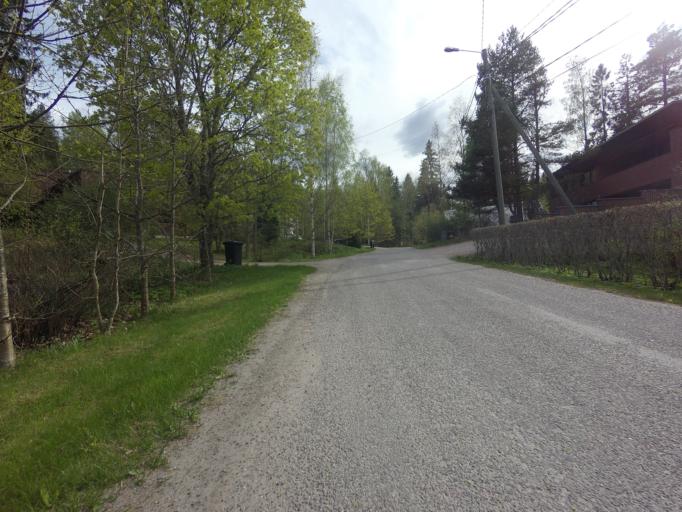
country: FI
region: Uusimaa
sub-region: Helsinki
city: Kauniainen
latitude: 60.1848
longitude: 24.7176
